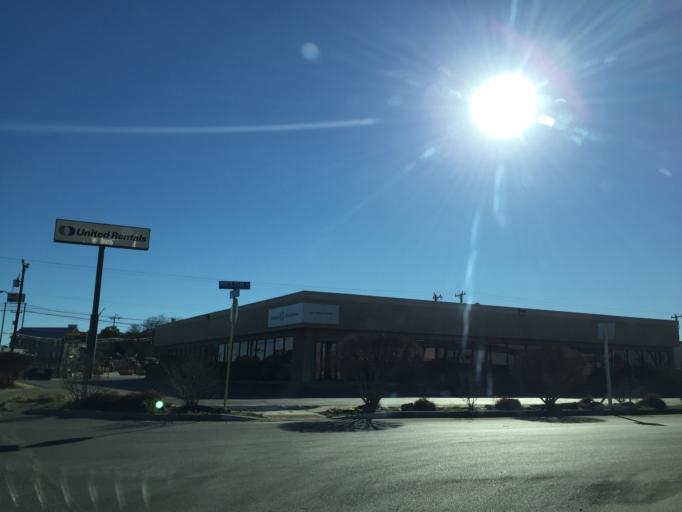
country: US
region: Texas
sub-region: Bexar County
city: Castle Hills
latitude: 29.5523
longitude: -98.4884
